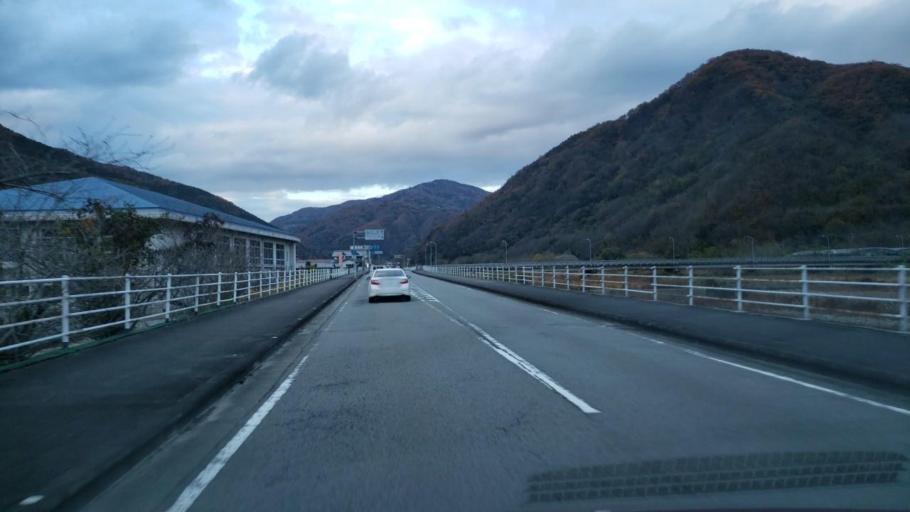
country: JP
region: Tokushima
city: Wakimachi
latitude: 34.0889
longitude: 134.1730
